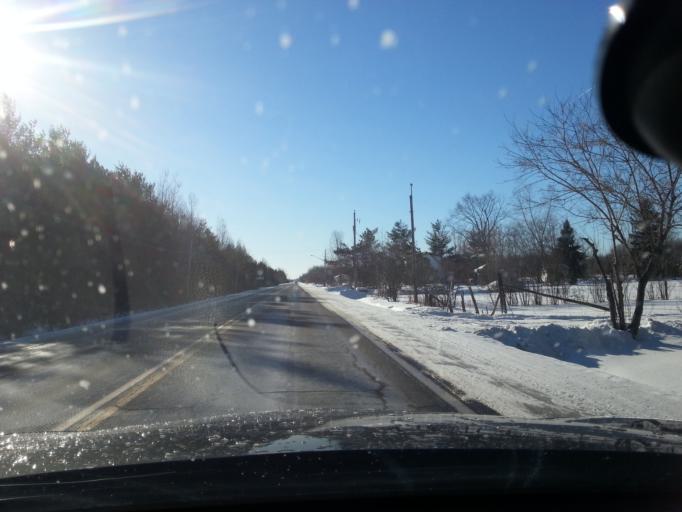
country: CA
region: Ontario
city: Ottawa
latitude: 45.3203
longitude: -75.4728
